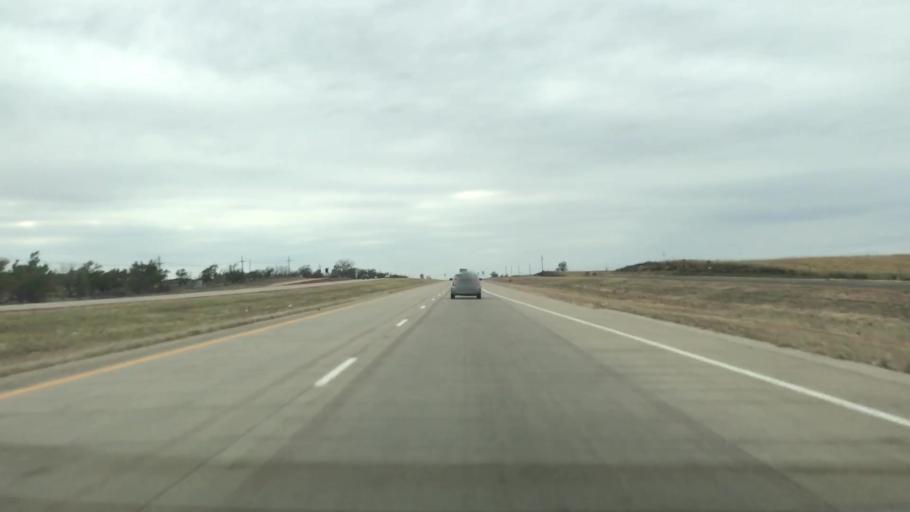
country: US
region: Texas
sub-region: Wheeler County
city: Shamrock
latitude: 35.2270
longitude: -100.1750
